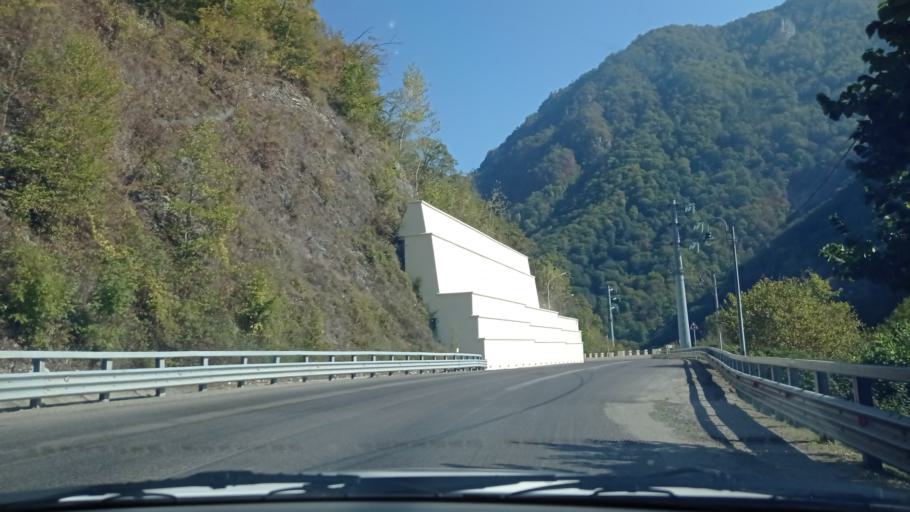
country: RU
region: Krasnodarskiy
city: Vysokoye
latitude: 43.5937
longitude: 40.0146
